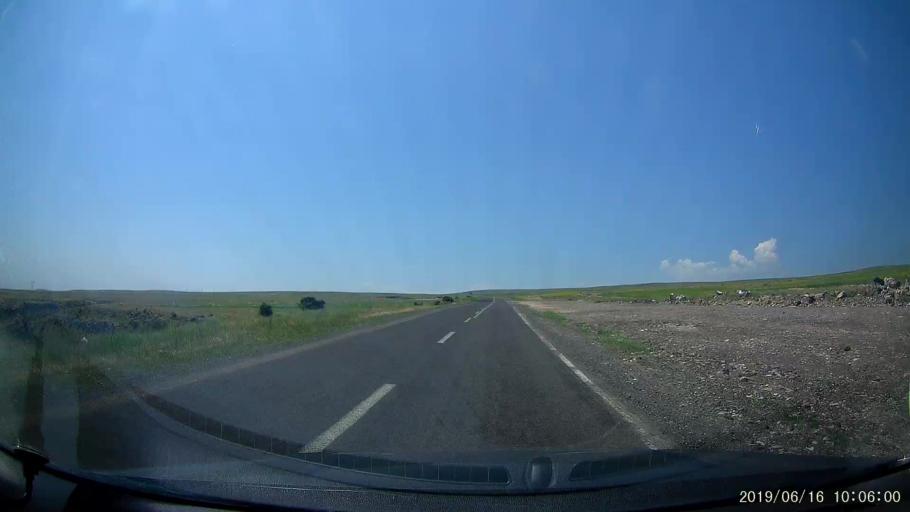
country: TR
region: Kars
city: Digor
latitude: 40.2620
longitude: 43.5403
